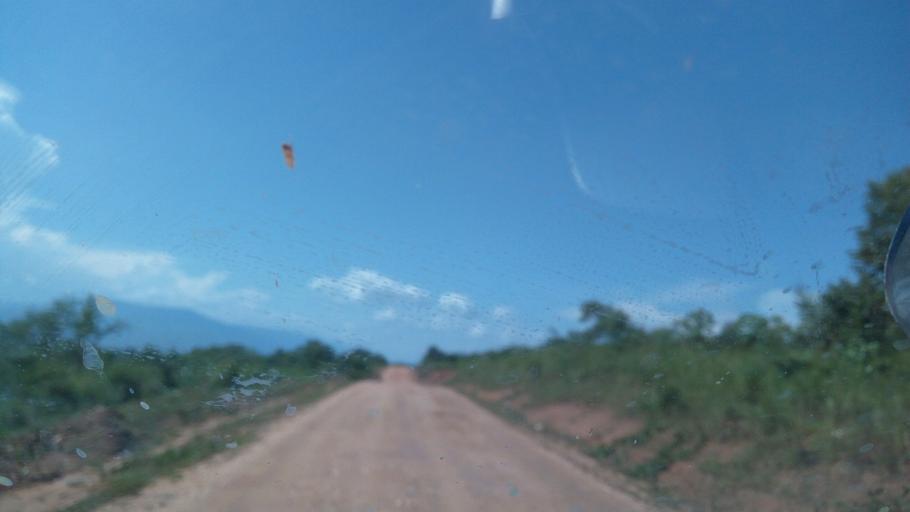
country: TZ
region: Kigoma
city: Kigoma
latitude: -4.6014
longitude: 28.7844
